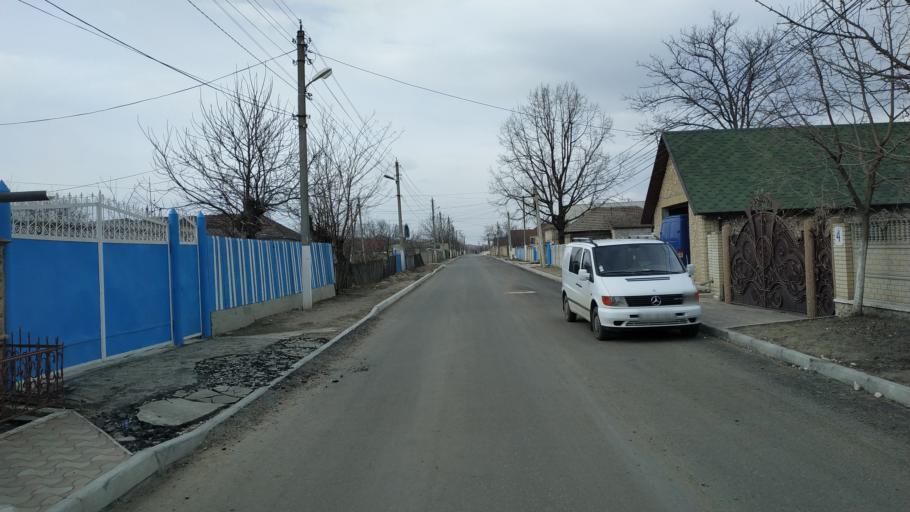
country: MD
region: Laloveni
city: Ialoveni
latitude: 46.8600
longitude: 28.7852
